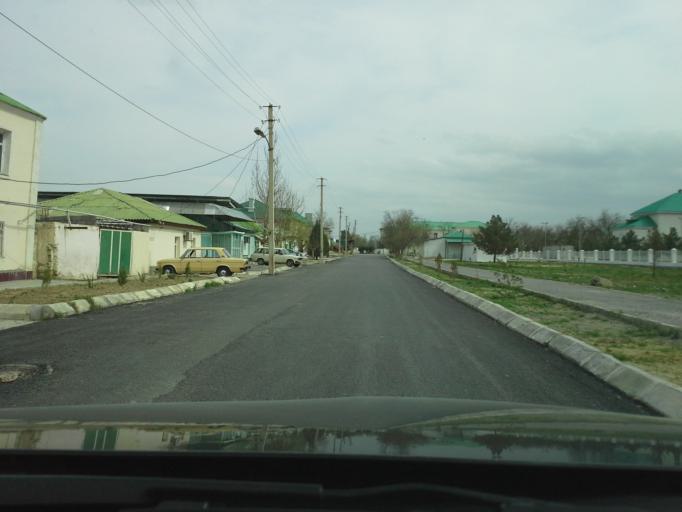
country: TM
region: Ahal
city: Abadan
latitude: 38.0618
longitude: 58.1525
